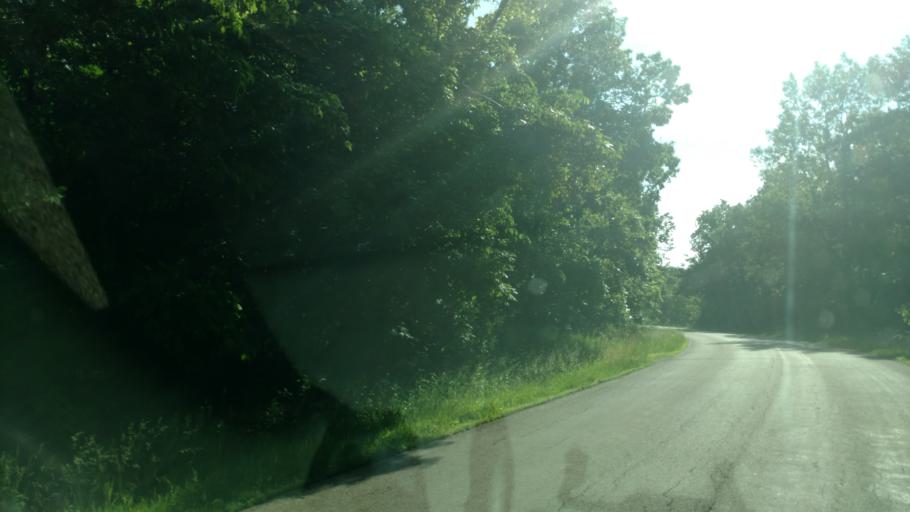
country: US
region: Wisconsin
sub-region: Vernon County
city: Hillsboro
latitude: 43.5840
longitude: -90.1956
